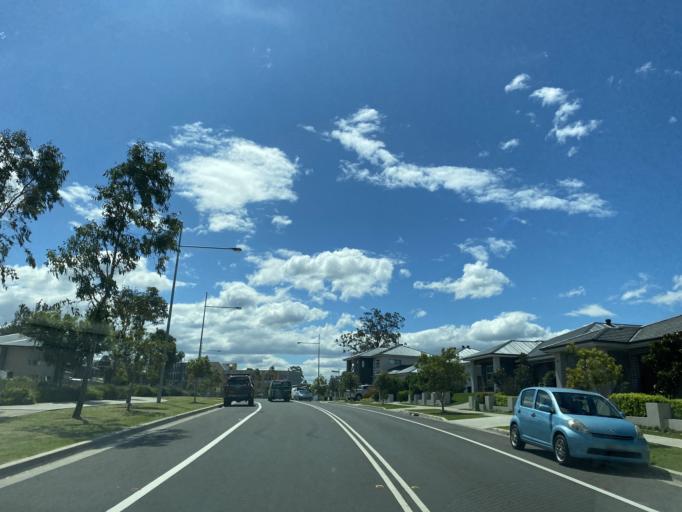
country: AU
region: New South Wales
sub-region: Camden
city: Narellan
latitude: -34.0149
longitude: 150.7771
